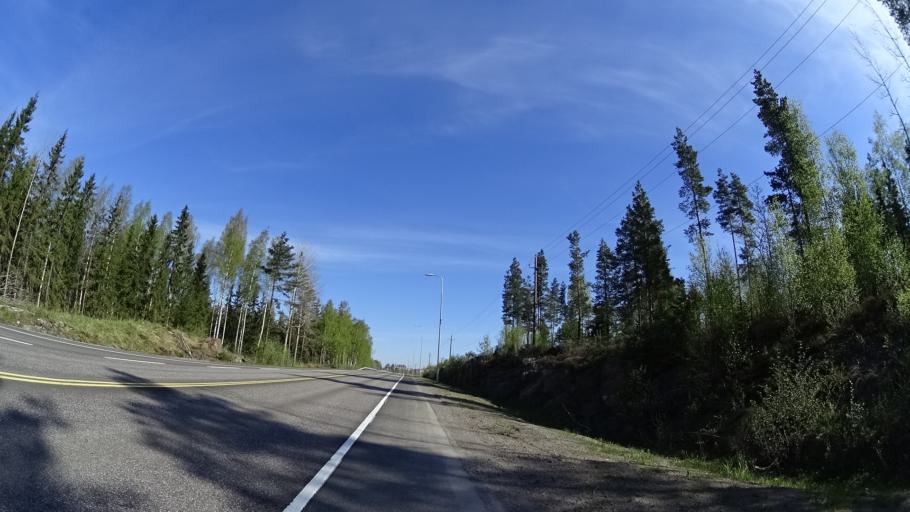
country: FI
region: Uusimaa
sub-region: Helsinki
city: Nurmijaervi
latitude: 60.4443
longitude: 24.8333
